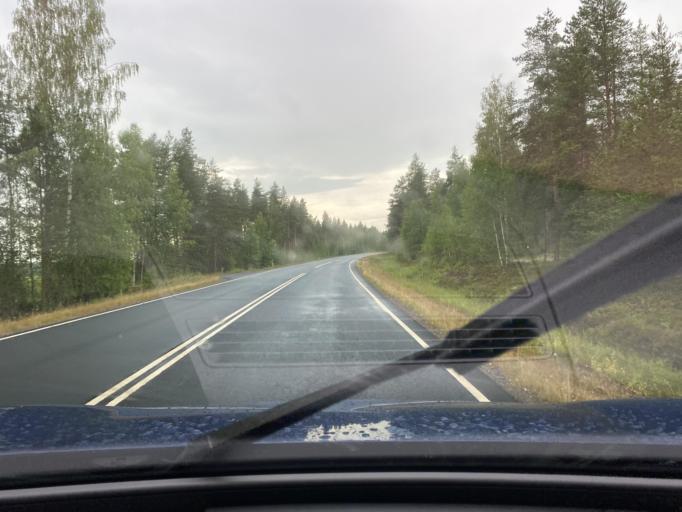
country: FI
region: Central Ostrobothnia
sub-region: Kaustinen
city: Veteli
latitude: 63.4111
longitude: 23.9587
